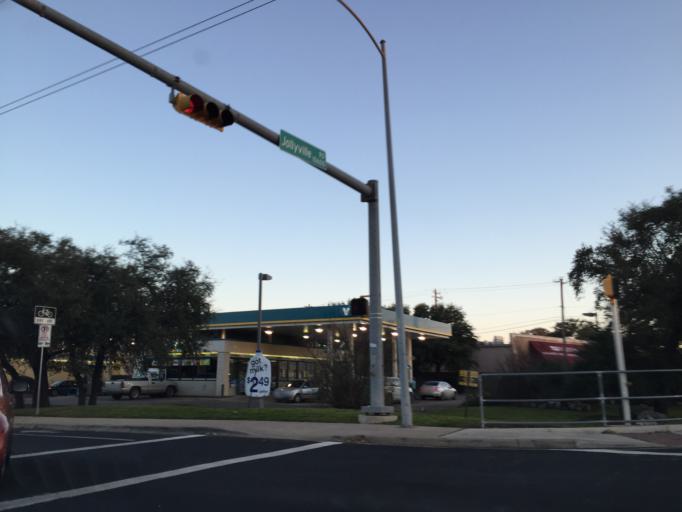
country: US
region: Texas
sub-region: Williamson County
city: Jollyville
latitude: 30.4008
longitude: -97.7488
